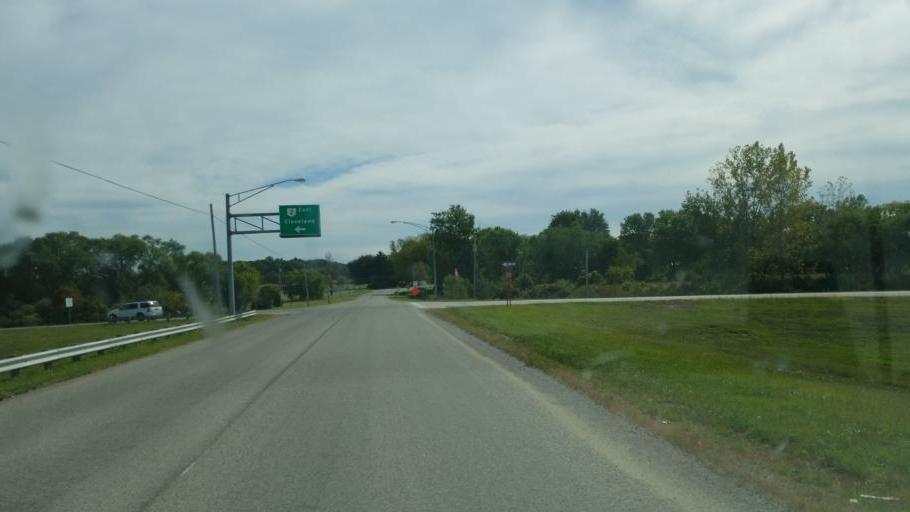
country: US
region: Ohio
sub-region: Erie County
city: Huron
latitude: 41.3673
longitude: -82.5205
